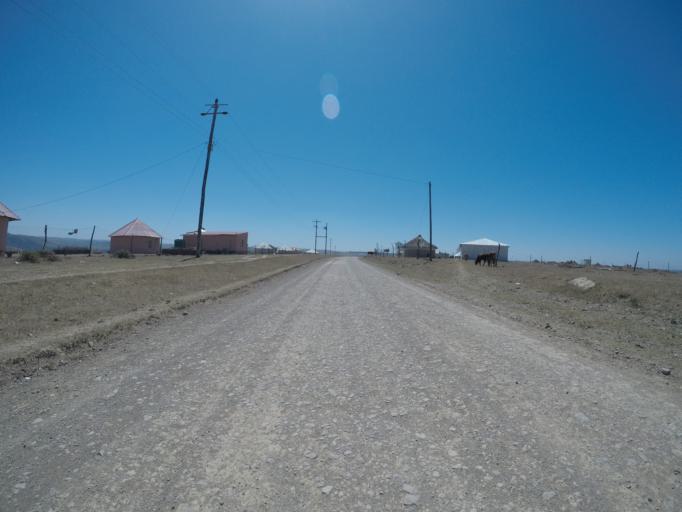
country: ZA
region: Eastern Cape
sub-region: OR Tambo District Municipality
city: Mthatha
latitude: -31.8842
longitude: 28.8750
